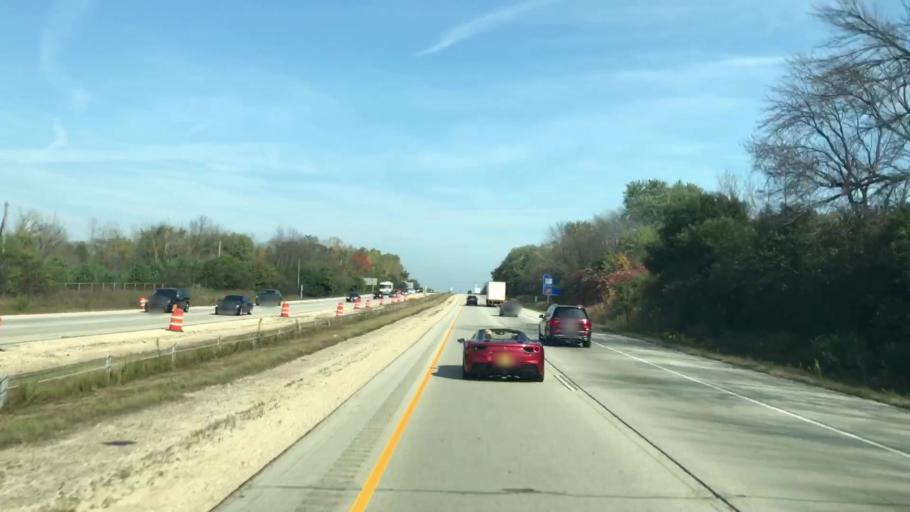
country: US
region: Wisconsin
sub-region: Milwaukee County
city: Fox Point
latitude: 43.1574
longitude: -87.9159
